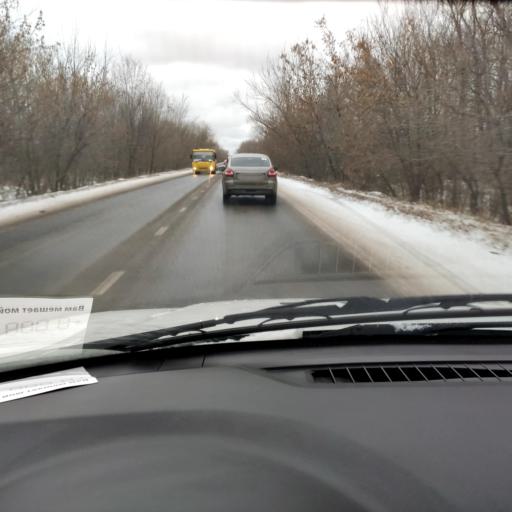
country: RU
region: Samara
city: Tol'yatti
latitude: 53.5498
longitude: 49.3937
